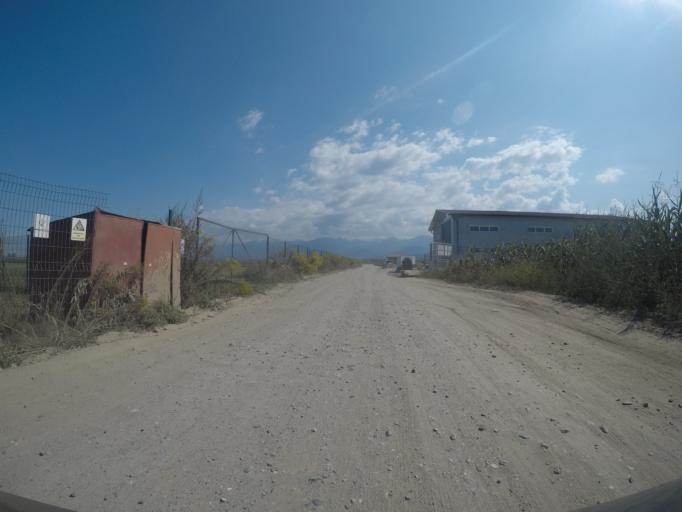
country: RO
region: Sibiu
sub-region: Comuna Avrig
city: Avrig
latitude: 45.7348
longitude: 24.3873
